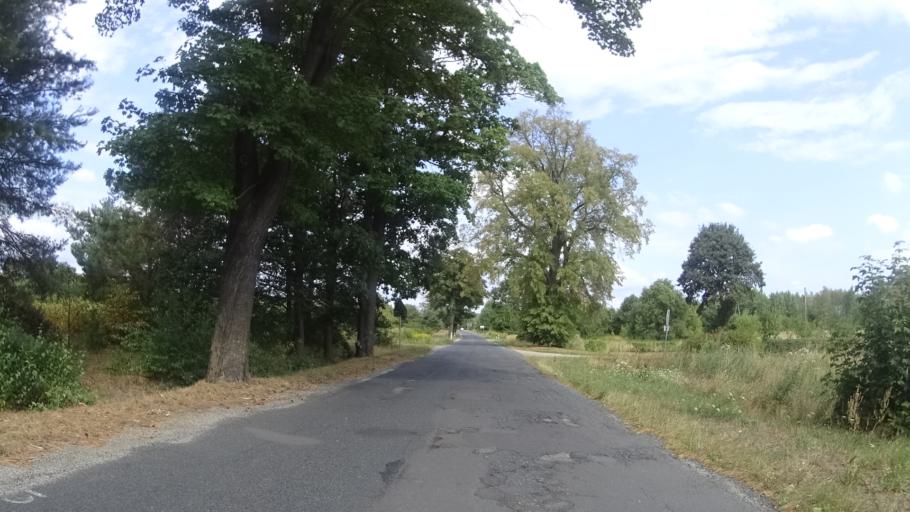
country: PL
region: Lubusz
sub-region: Powiat zarski
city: Leknica
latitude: 51.5353
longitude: 14.8067
